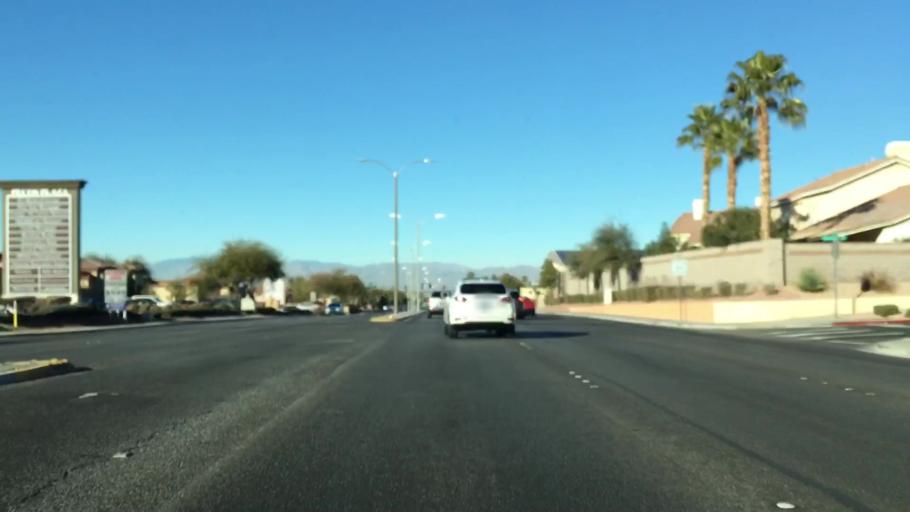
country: US
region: Nevada
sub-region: Clark County
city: Whitney
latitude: 36.0255
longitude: -115.1005
